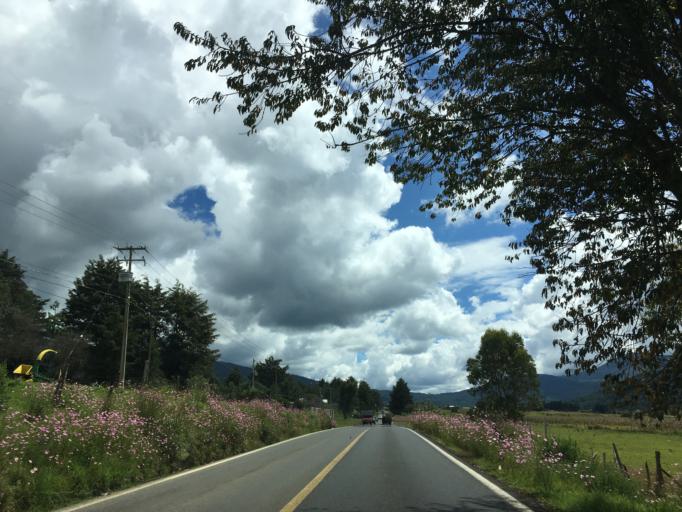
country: MX
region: Michoacan
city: Nahuatzen
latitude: 19.6607
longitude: -101.9328
